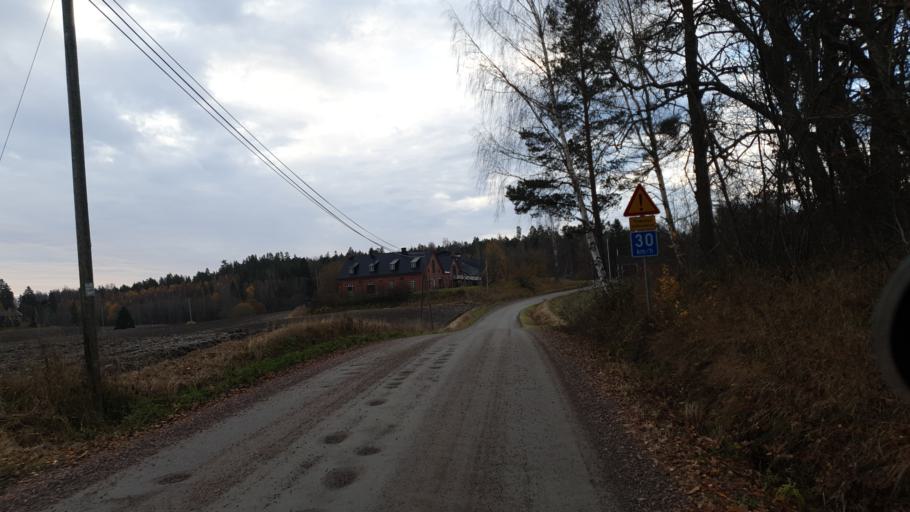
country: FI
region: Uusimaa
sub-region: Helsinki
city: Siuntio
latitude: 60.1228
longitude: 24.2882
